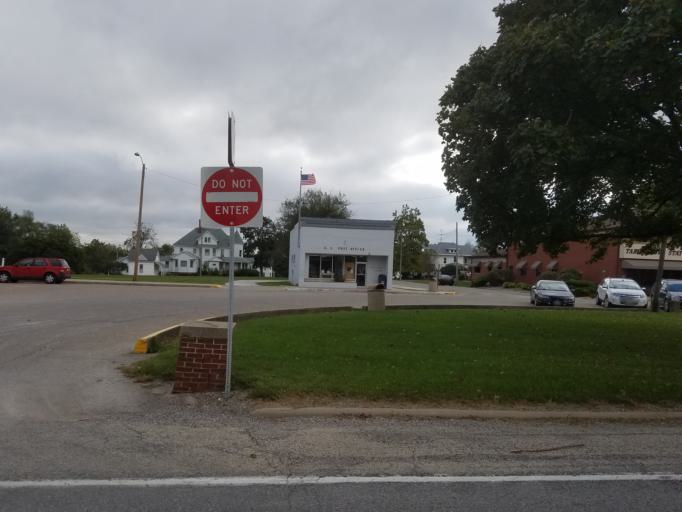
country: US
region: Illinois
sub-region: Fulton County
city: Astoria
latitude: 40.3659
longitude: -90.4252
